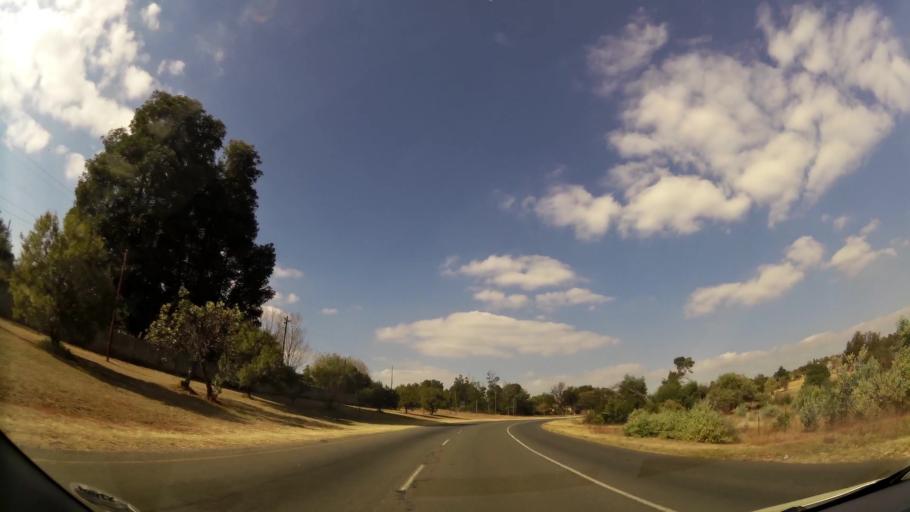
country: ZA
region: Gauteng
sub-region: West Rand District Municipality
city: Krugersdorp
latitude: -26.0455
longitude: 27.7524
